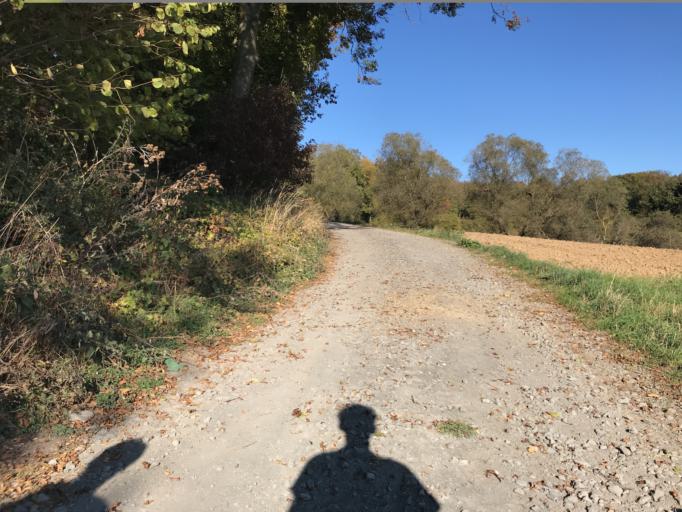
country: DE
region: Rheinland-Pfalz
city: Wolken
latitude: 50.3371
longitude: 7.4455
